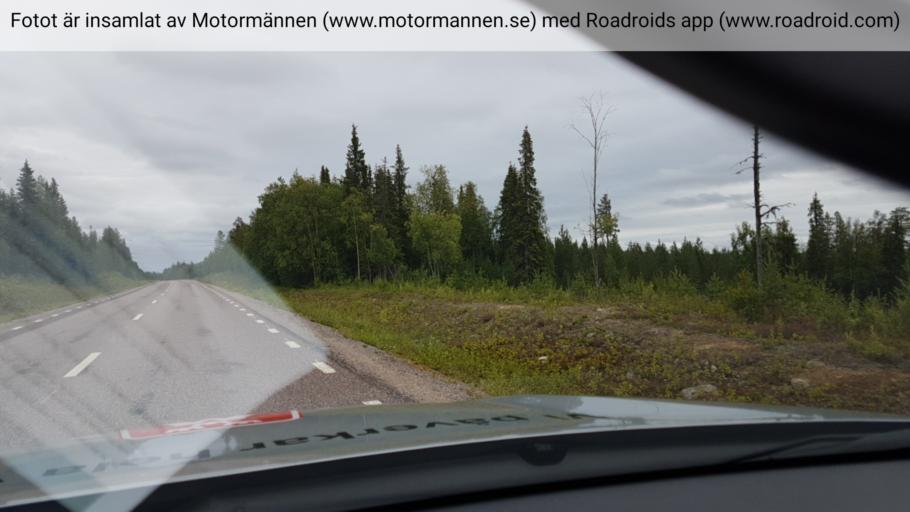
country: SE
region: Norrbotten
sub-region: Gallivare Kommun
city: Gaellivare
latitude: 67.0754
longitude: 21.4342
